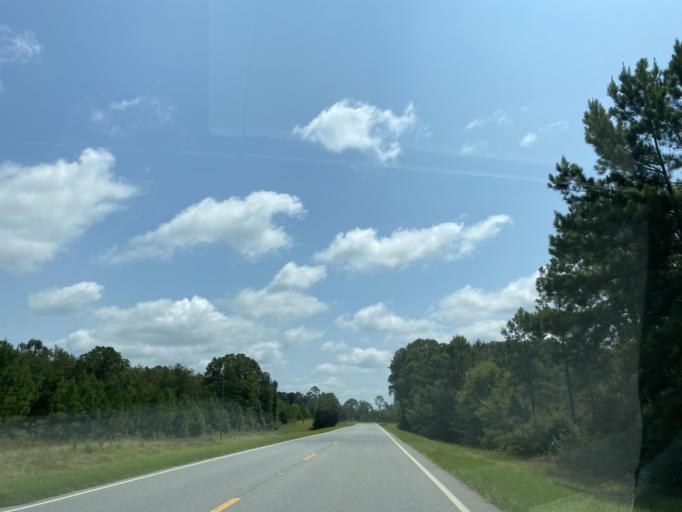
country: US
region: Georgia
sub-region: Telfair County
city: Helena
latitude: 32.0296
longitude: -83.0140
